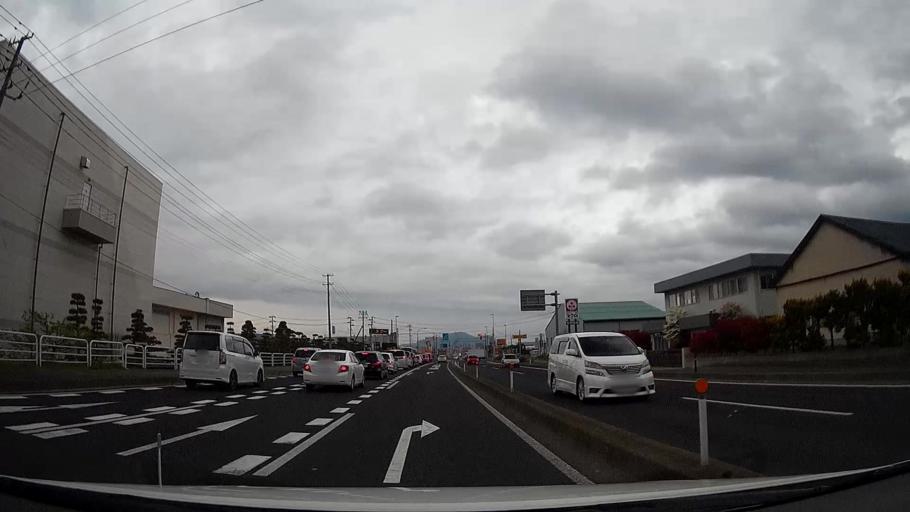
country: JP
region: Yamagata
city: Tendo
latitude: 38.3228
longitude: 140.3635
